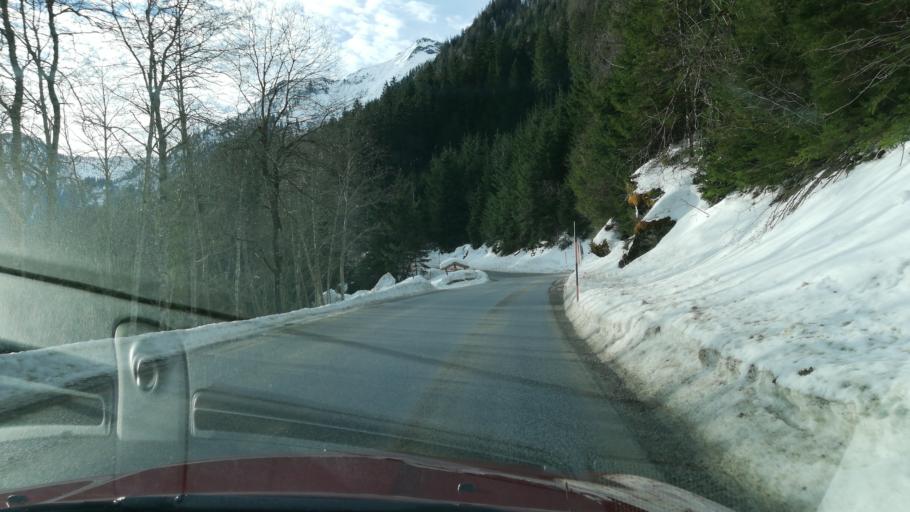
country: AT
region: Styria
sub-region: Politischer Bezirk Liezen
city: Donnersbach
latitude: 47.4254
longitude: 14.1653
